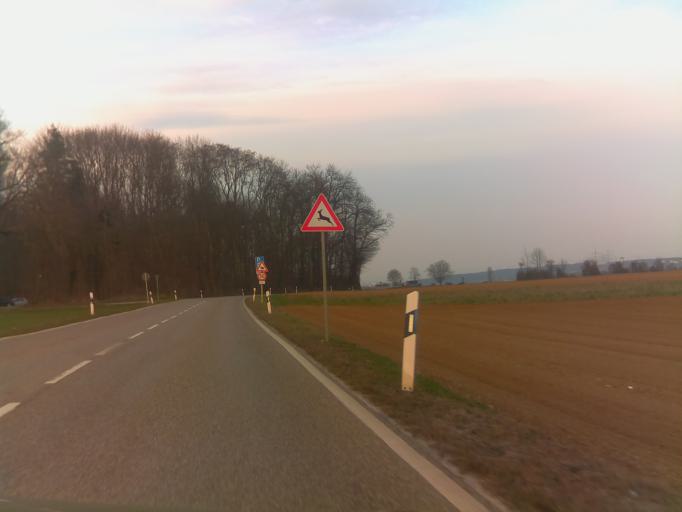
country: DE
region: Baden-Wuerttemberg
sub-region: Regierungsbezirk Stuttgart
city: Oberriexingen
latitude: 48.8968
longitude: 9.0150
